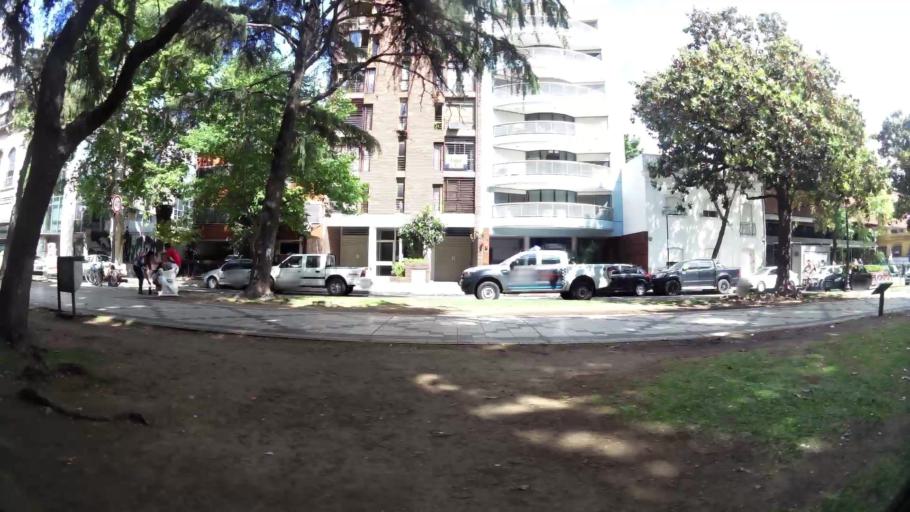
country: AR
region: Santa Fe
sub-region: Departamento de Rosario
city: Rosario
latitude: -32.9361
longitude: -60.6515
